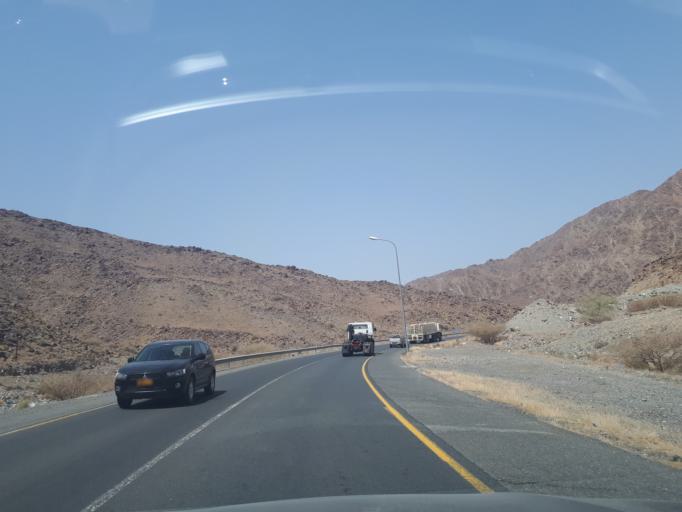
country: OM
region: Muhafazat ad Dakhiliyah
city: Sufalat Sama'il
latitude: 23.2494
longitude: 58.0960
